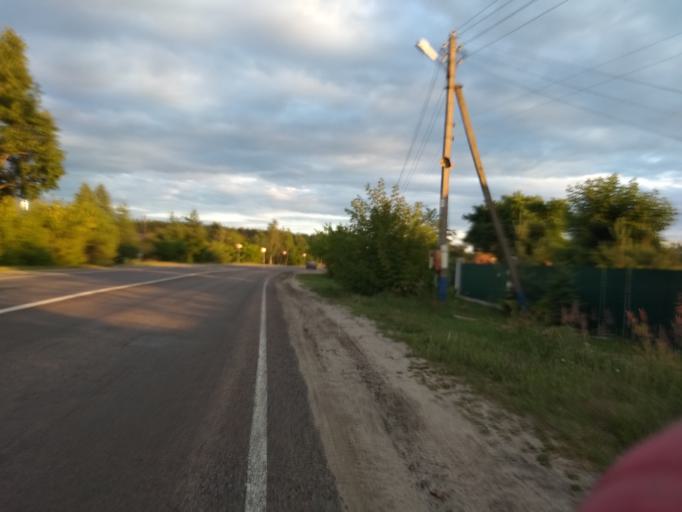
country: RU
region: Moskovskaya
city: Kerva
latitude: 55.5886
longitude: 39.7010
